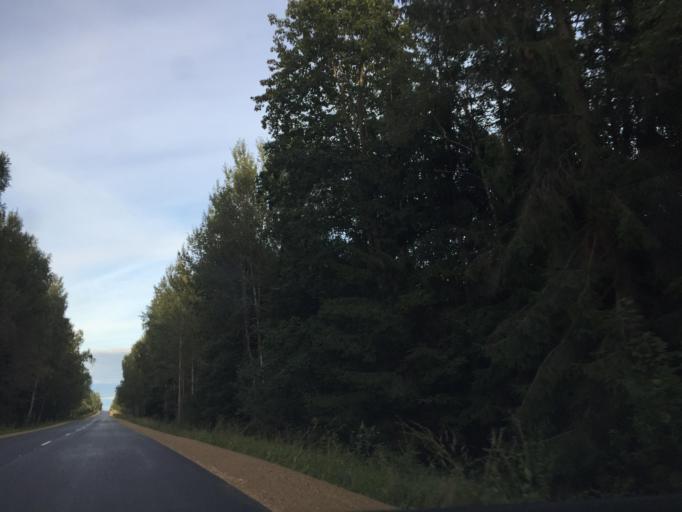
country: LV
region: Viesite
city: Viesite
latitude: 56.3486
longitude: 25.5840
